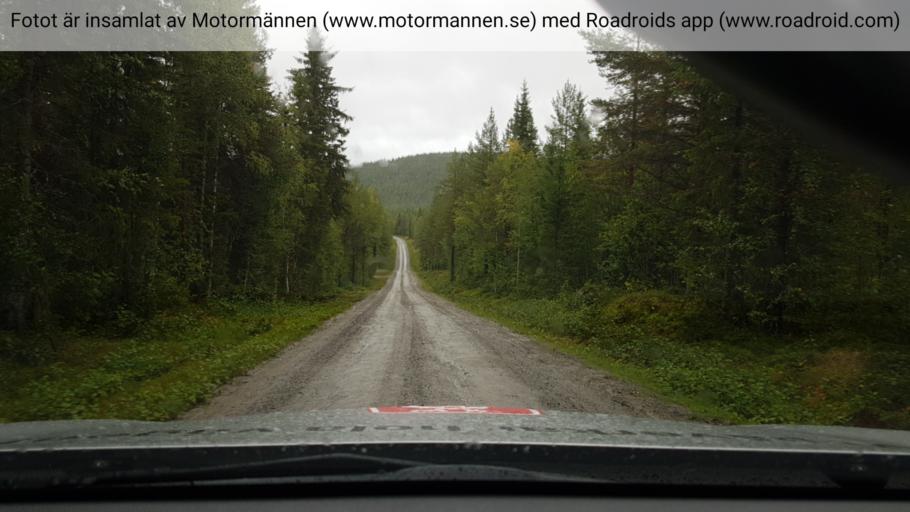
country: SE
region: Vaesterbotten
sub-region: Asele Kommun
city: Asele
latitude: 63.9934
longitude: 17.5977
